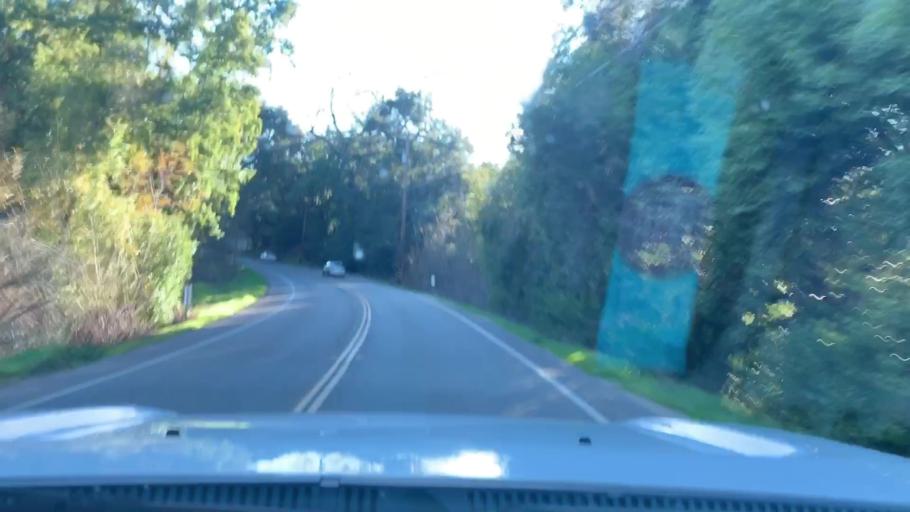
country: US
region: California
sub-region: San Luis Obispo County
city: Atascadero
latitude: 35.4572
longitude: -120.7505
